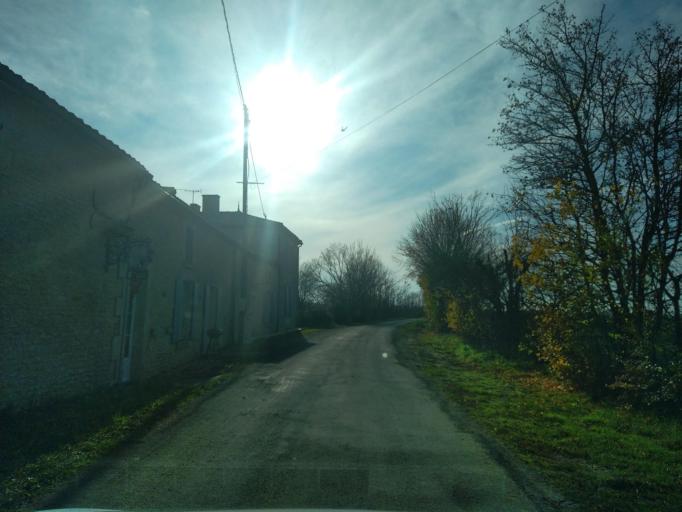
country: FR
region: Pays de la Loire
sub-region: Departement de la Vendee
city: Maillezais
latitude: 46.3552
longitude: -0.7416
